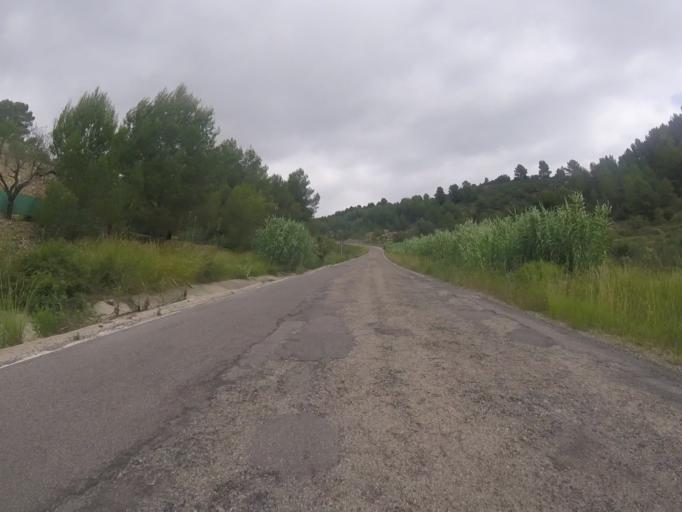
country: ES
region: Valencia
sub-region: Provincia de Castello
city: Cabanes
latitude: 40.1174
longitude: 0.0475
